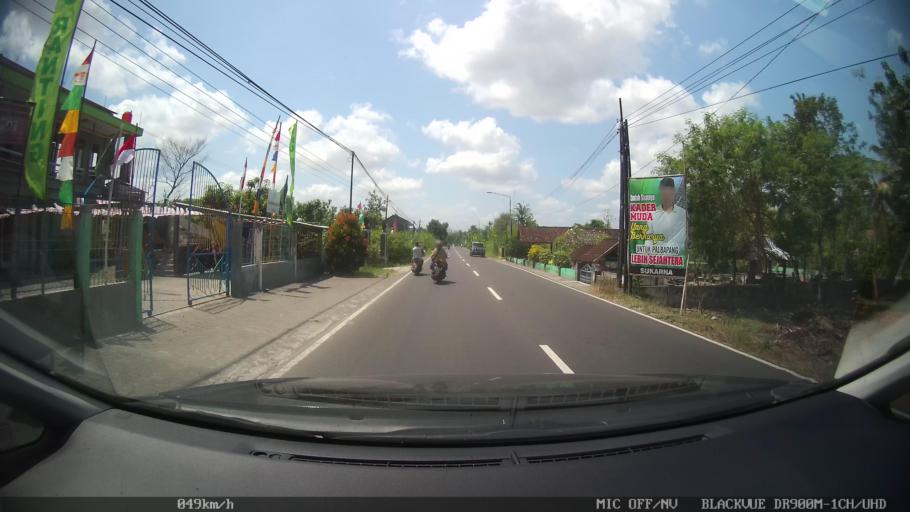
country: ID
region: Daerah Istimewa Yogyakarta
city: Bantul
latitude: -7.9050
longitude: 110.3258
